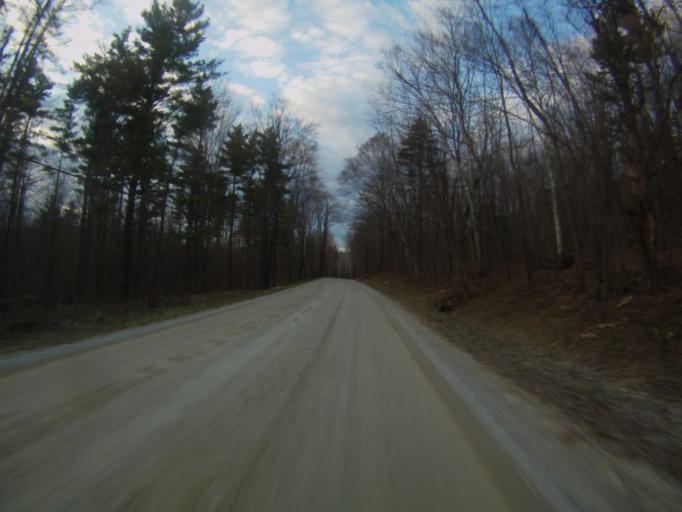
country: US
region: Vermont
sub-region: Rutland County
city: Brandon
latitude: 43.8834
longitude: -73.0120
